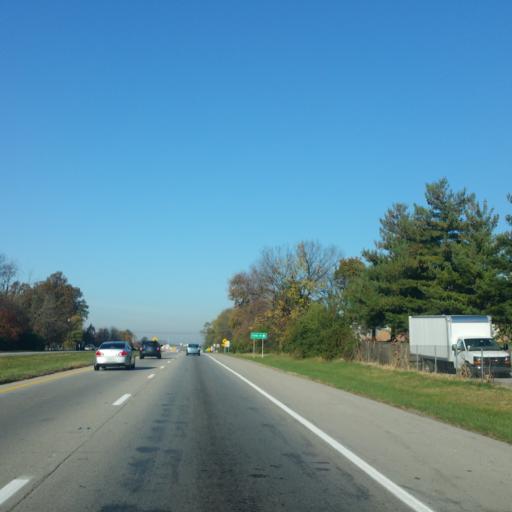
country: US
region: Ohio
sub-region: Clermont County
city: Summerside
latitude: 39.0928
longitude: -84.2551
